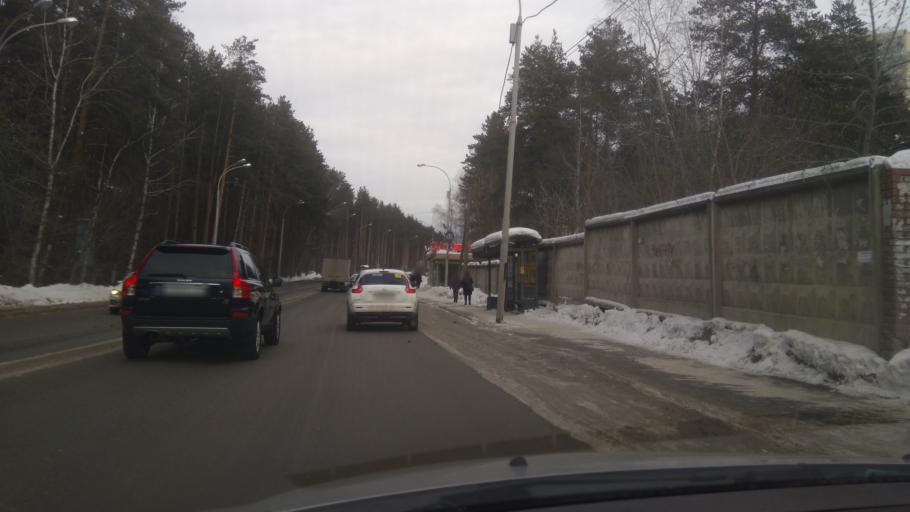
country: RU
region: Sverdlovsk
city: Shirokaya Rechka
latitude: 56.8106
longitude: 60.5089
